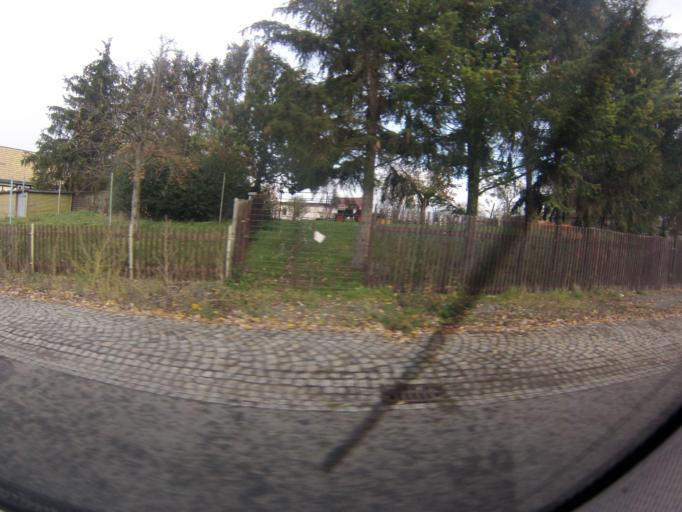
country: DE
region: Thuringia
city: Schmolln
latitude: 50.8834
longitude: 12.3860
